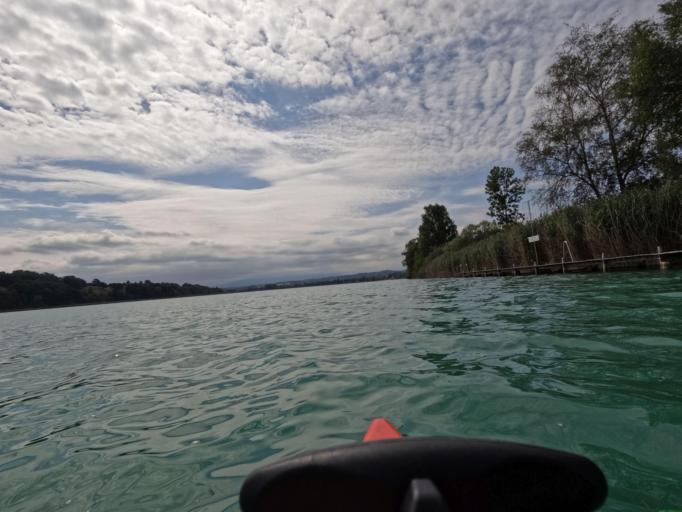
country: DE
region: Bavaria
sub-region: Upper Bavaria
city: Taching am See
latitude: 47.9703
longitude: 12.7402
